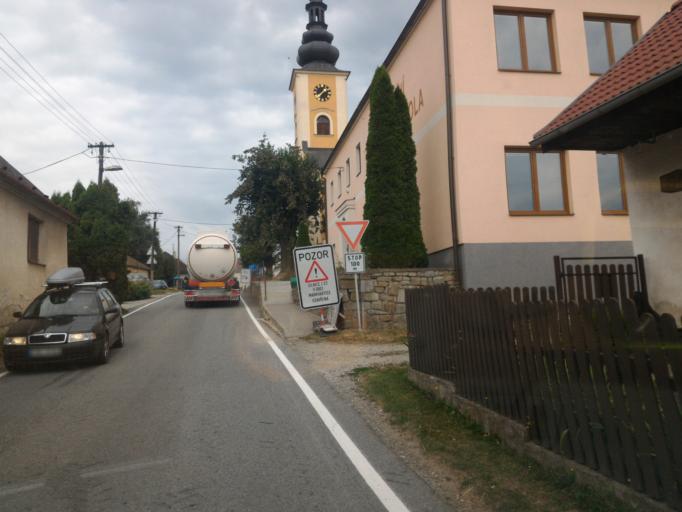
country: CZ
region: Vysocina
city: Zeletava
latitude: 49.1760
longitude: 15.5949
